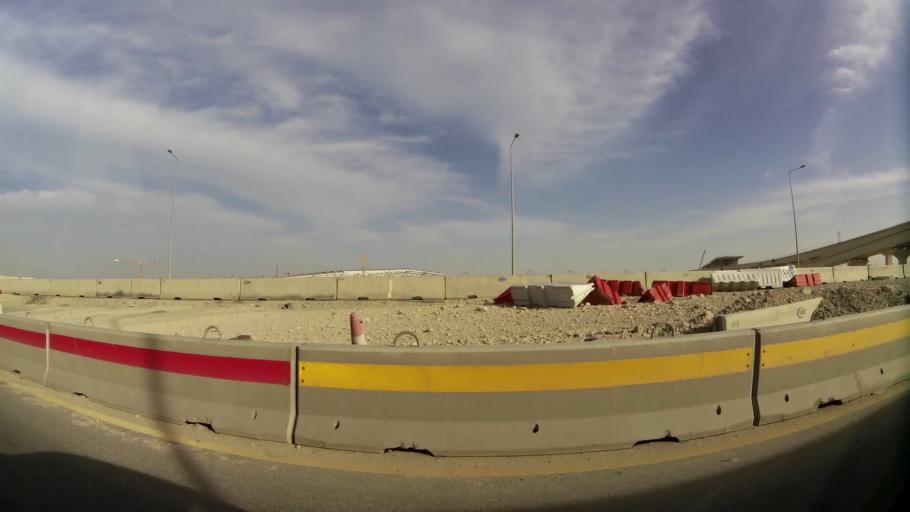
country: QA
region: Al Wakrah
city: Al Wakrah
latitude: 25.2154
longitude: 51.5850
